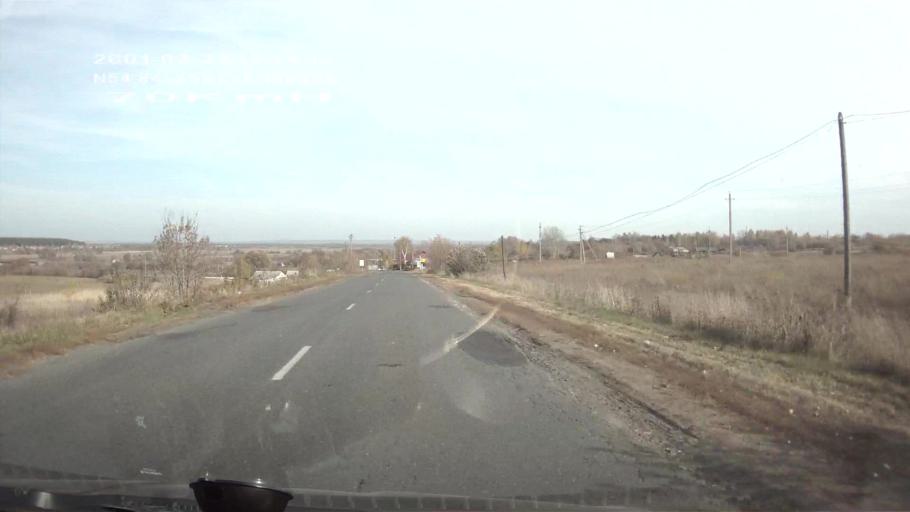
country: RU
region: Chuvashia
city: Alatyr'
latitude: 54.8458
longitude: 46.4892
